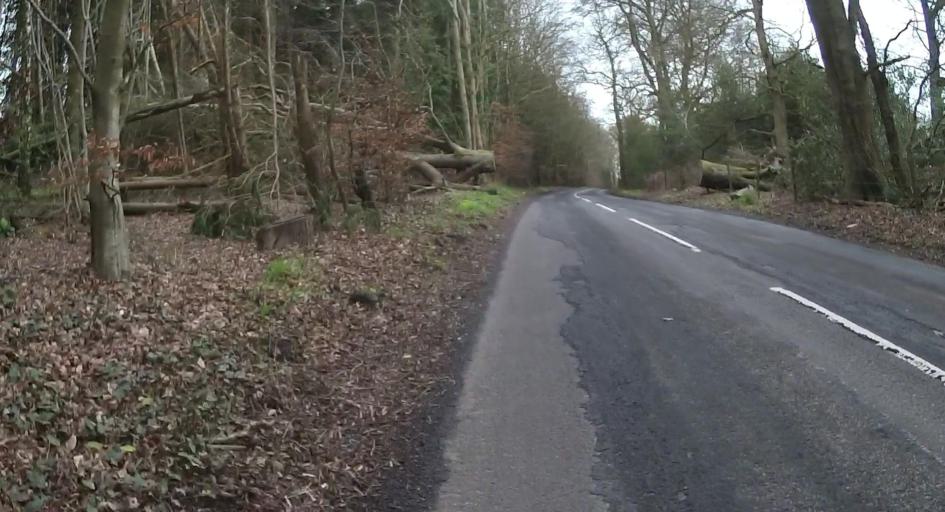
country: GB
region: England
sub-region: Hampshire
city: Alton
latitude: 51.1807
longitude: -0.9846
